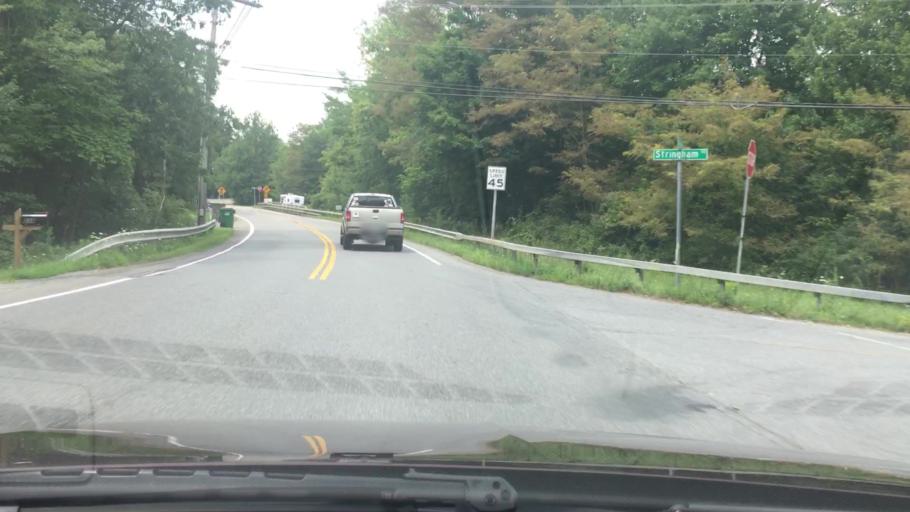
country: US
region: New York
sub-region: Dutchess County
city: Hillside Lake
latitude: 41.6444
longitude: -73.8096
